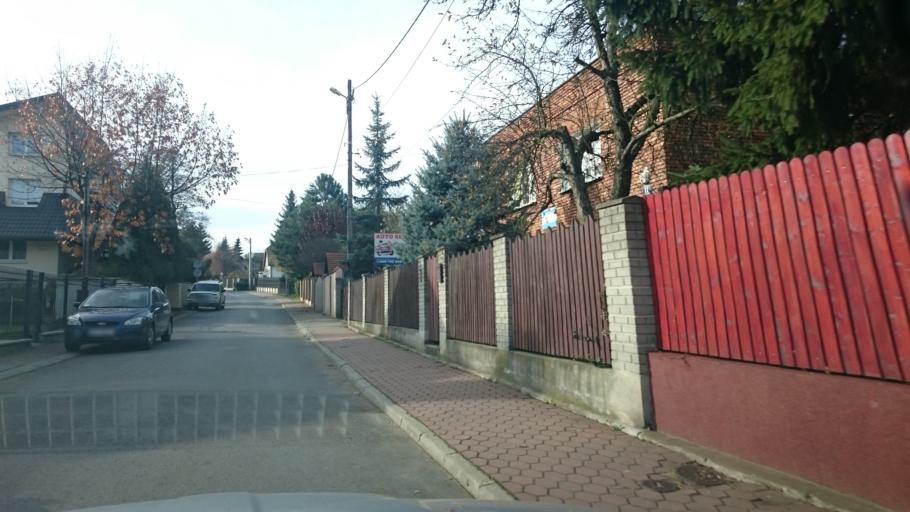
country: PL
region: Lesser Poland Voivodeship
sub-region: Krakow
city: Krakow
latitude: 50.0253
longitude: 19.9665
